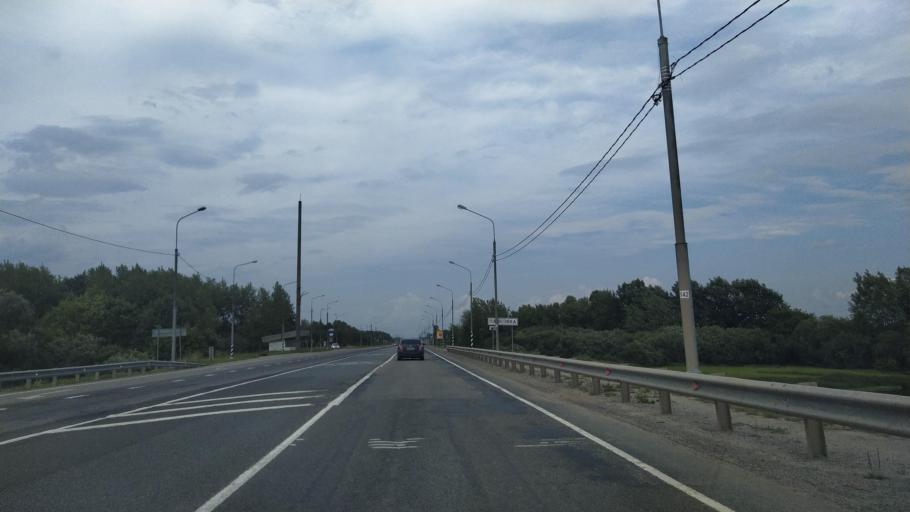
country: RU
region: Novgorod
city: Pankovka
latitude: 58.4725
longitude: 31.1711
